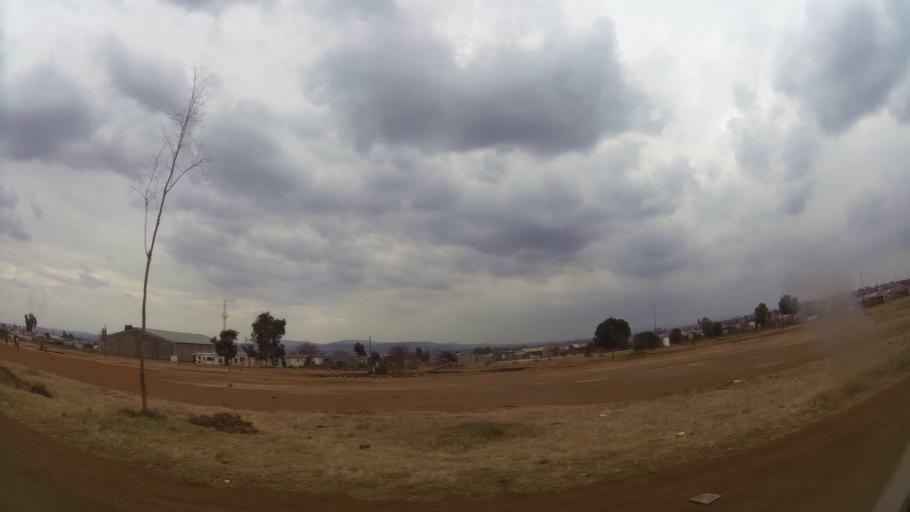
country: ZA
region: Gauteng
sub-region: Ekurhuleni Metropolitan Municipality
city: Germiston
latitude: -26.3917
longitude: 28.1343
